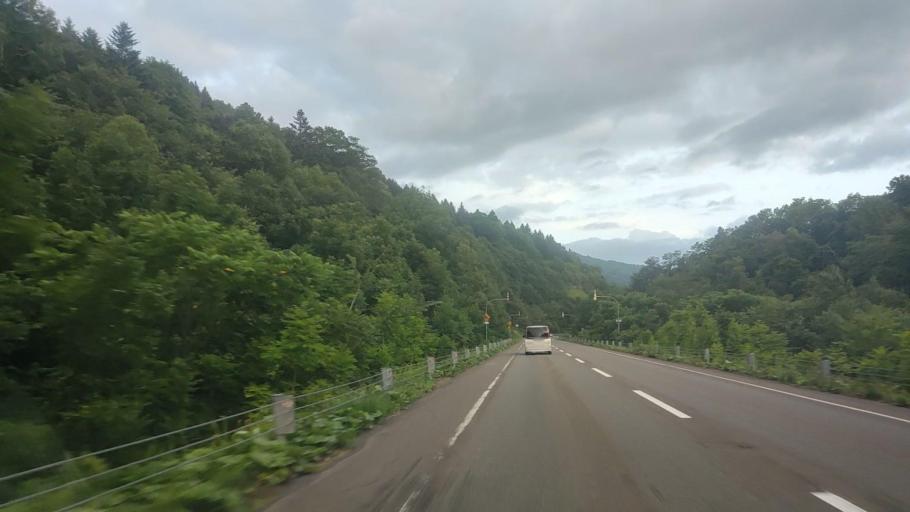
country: JP
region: Hokkaido
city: Shimo-furano
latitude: 43.3584
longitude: 142.2423
